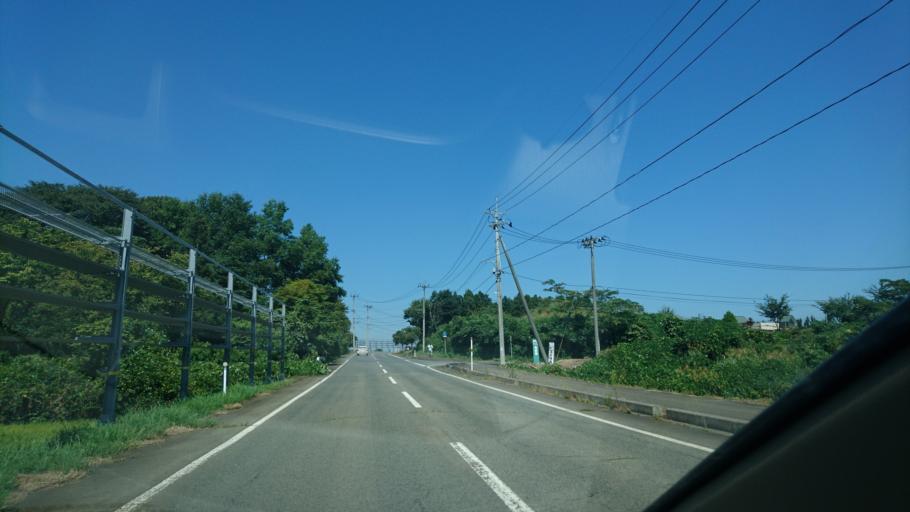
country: JP
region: Iwate
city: Kitakami
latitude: 39.2566
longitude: 141.0826
